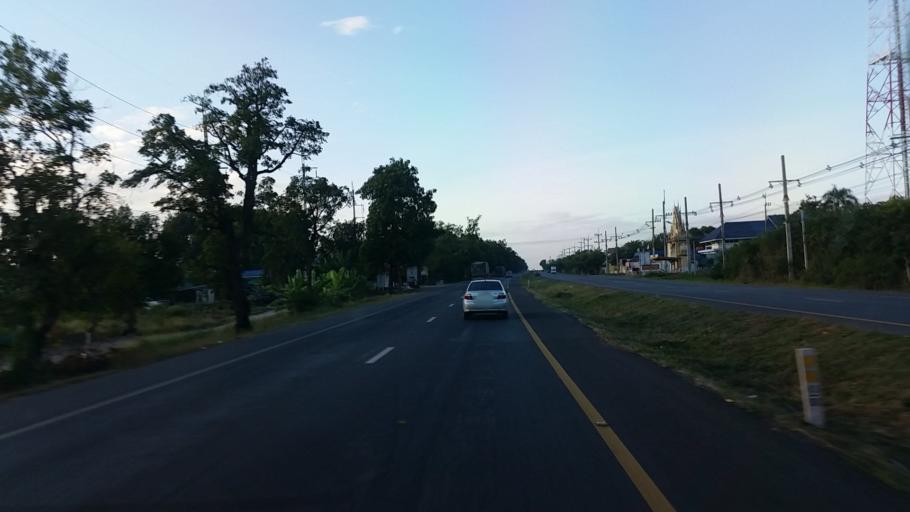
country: TH
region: Lop Buri
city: Chai Badan
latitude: 15.1655
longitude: 101.0624
